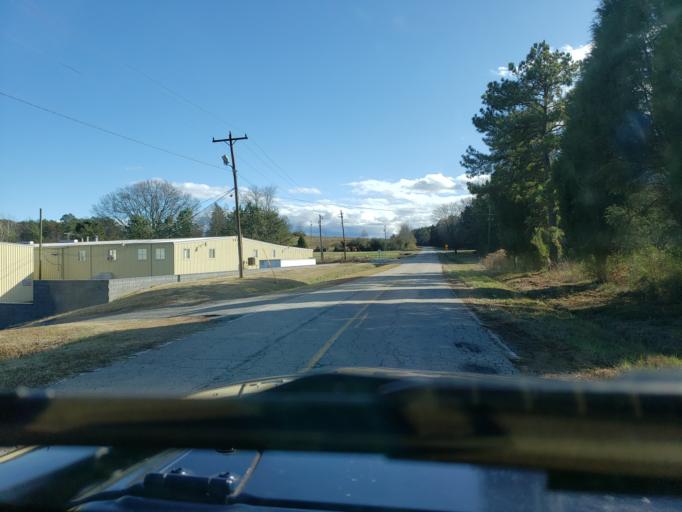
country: US
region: North Carolina
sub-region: Cleveland County
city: White Plains
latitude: 35.1663
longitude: -81.4266
